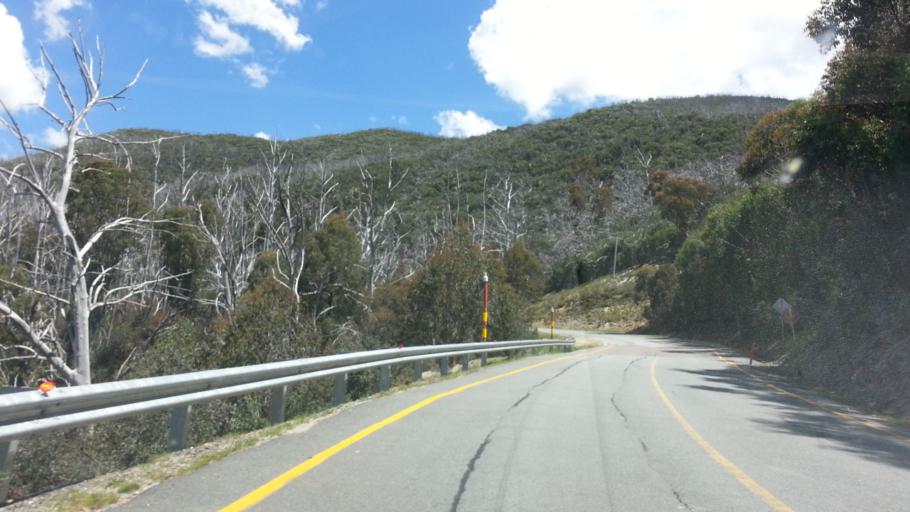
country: AU
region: Victoria
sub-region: Alpine
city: Mount Beauty
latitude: -36.8478
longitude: 147.2698
